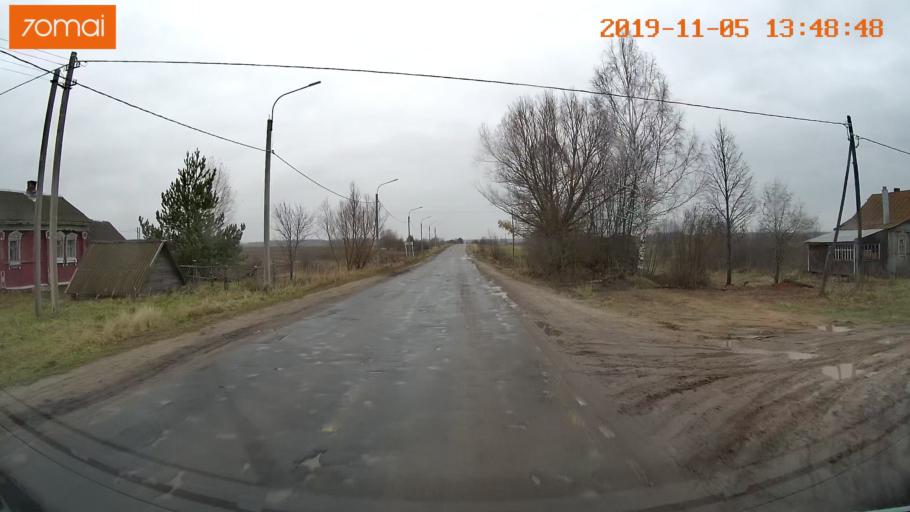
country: RU
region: Ivanovo
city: Shuya
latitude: 57.0054
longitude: 41.4074
